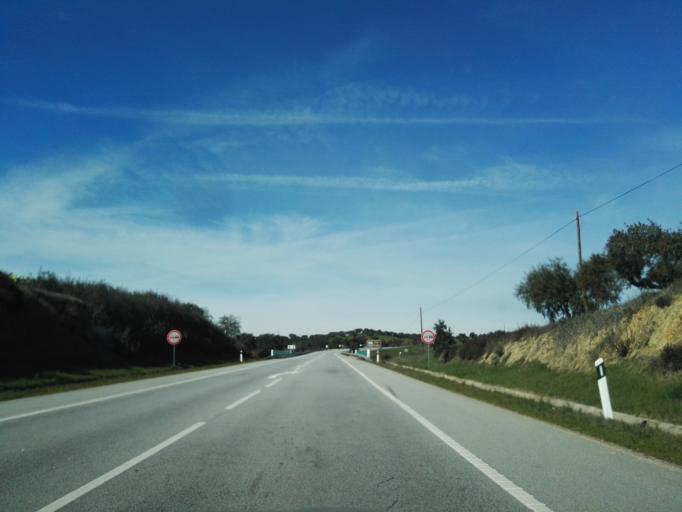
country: PT
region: Portalegre
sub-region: Portalegre
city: Urra
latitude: 39.1951
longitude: -7.3621
